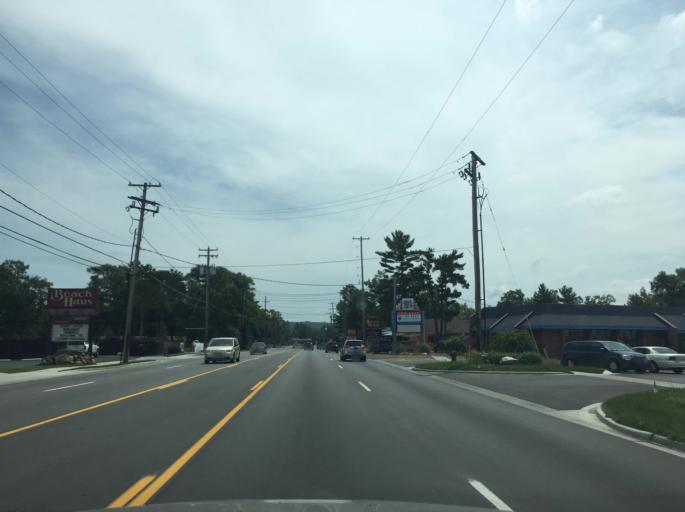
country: US
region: Michigan
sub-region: Grand Traverse County
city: Traverse City
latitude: 44.7466
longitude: -85.5469
